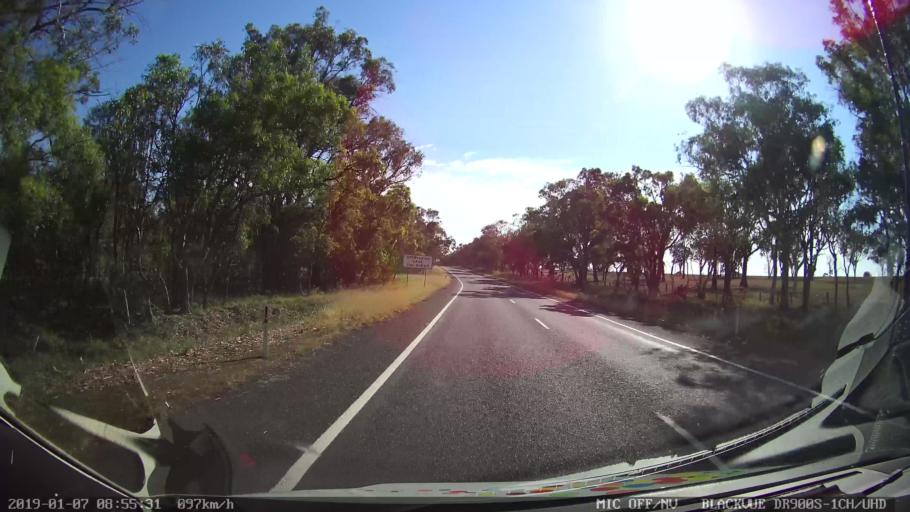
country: AU
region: New South Wales
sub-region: Tamworth Municipality
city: Kootingal
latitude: -30.7836
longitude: 151.3296
